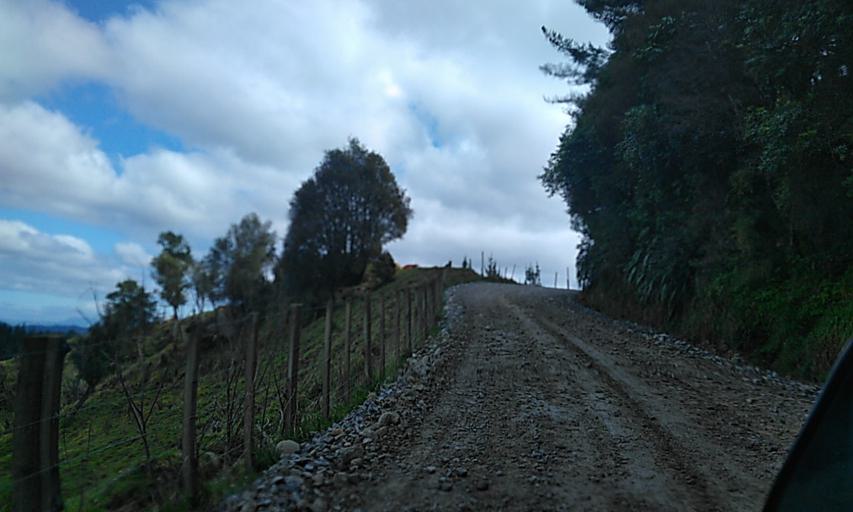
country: NZ
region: Gisborne
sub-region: Gisborne District
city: Gisborne
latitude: -38.3181
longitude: 178.0865
